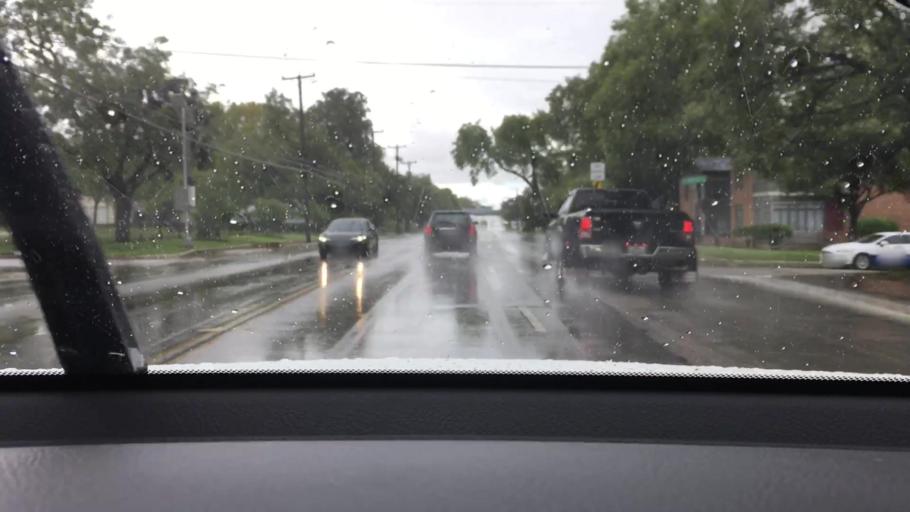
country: US
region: Texas
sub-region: Bexar County
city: Alamo Heights
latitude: 29.4895
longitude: -98.4666
